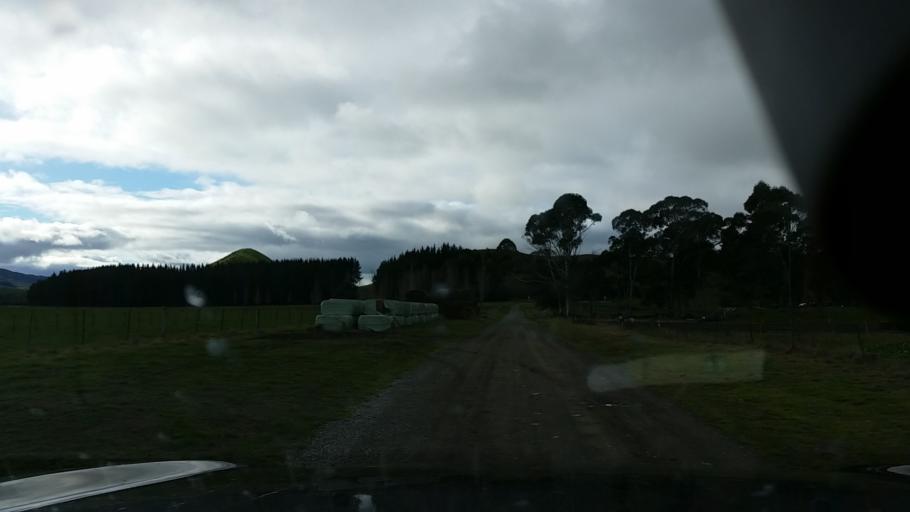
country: NZ
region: Marlborough
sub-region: Marlborough District
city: Blenheim
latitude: -41.6594
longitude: 173.6589
